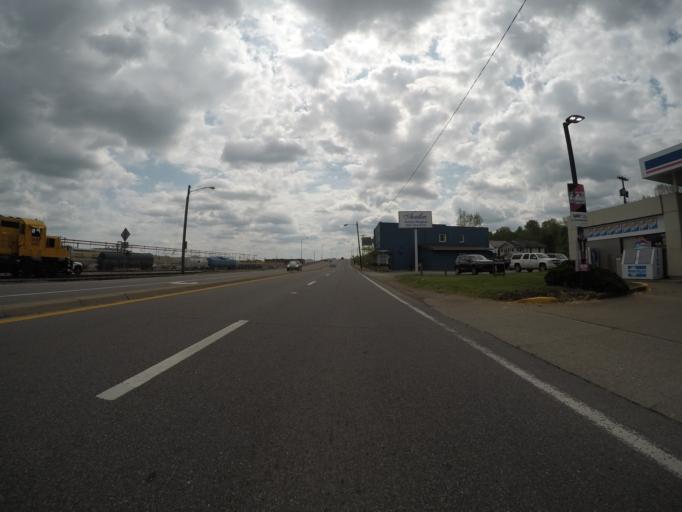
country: US
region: West Virginia
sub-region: Kanawha County
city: South Charleston
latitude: 38.3670
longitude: -81.6840
